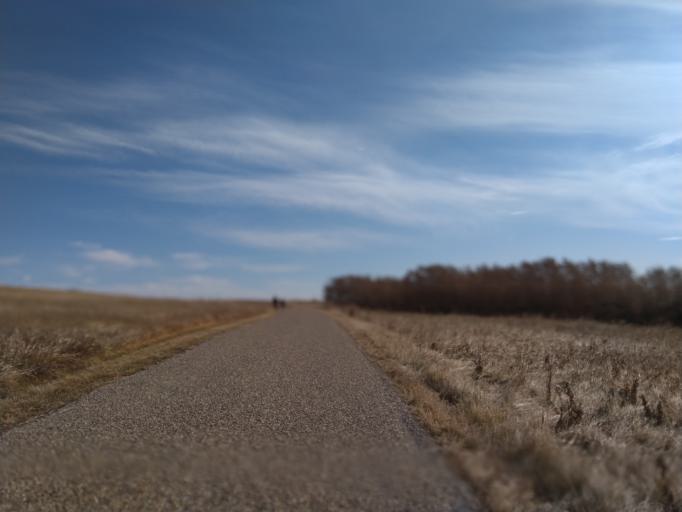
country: CA
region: Alberta
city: Calgary
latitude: 51.1114
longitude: -114.1248
